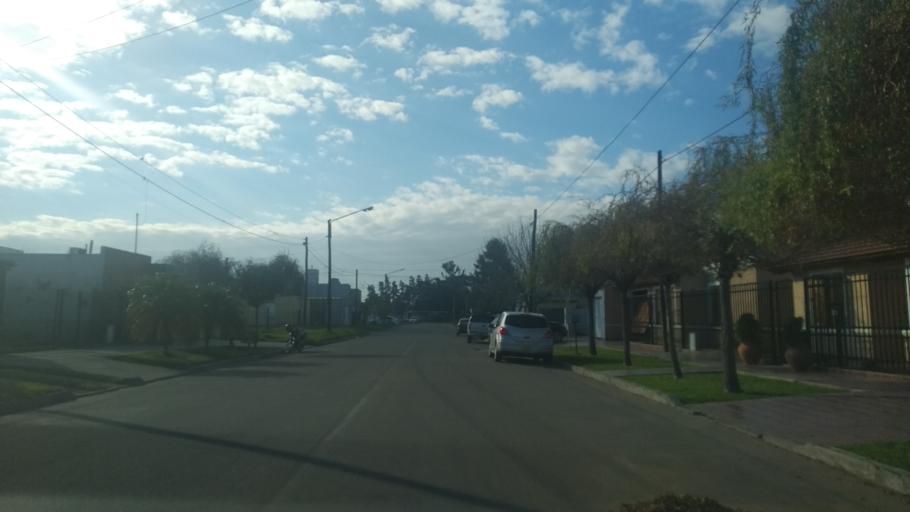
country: AR
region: Cordoba
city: Leones
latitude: -32.6561
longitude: -62.2929
